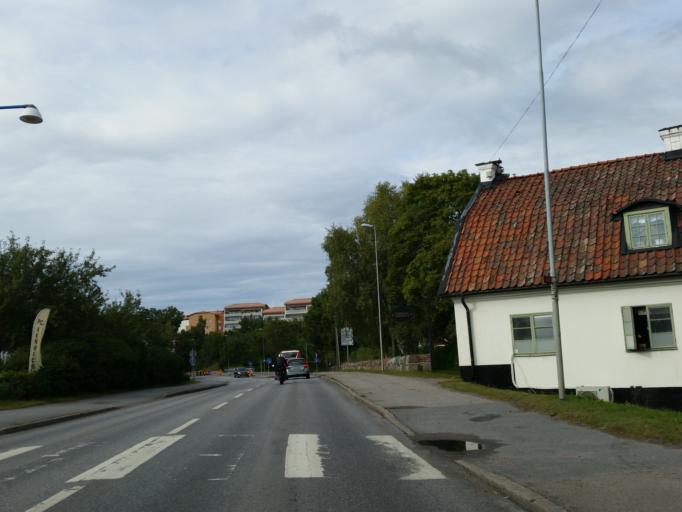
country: SE
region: Stockholm
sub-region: Sollentuna Kommun
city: Sollentuna
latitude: 59.4402
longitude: 17.9504
